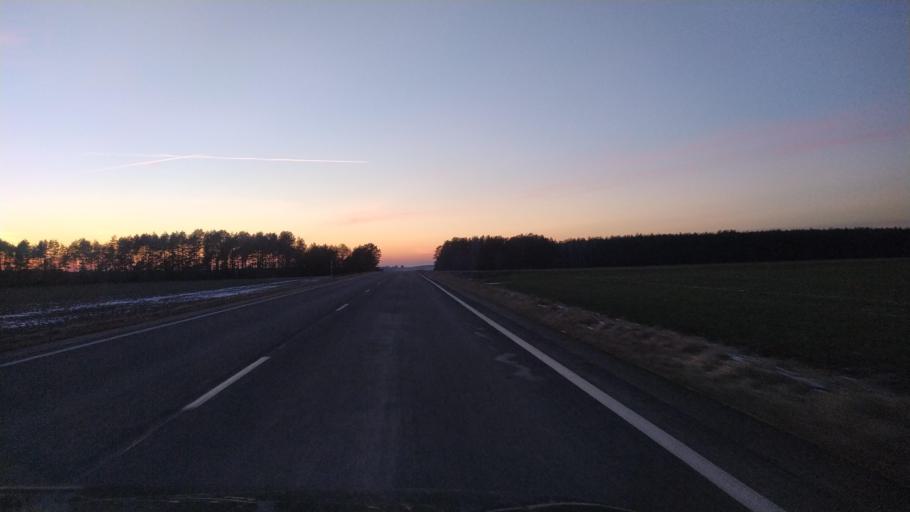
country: BY
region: Brest
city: Kamyanyets
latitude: 52.3948
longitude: 23.9286
